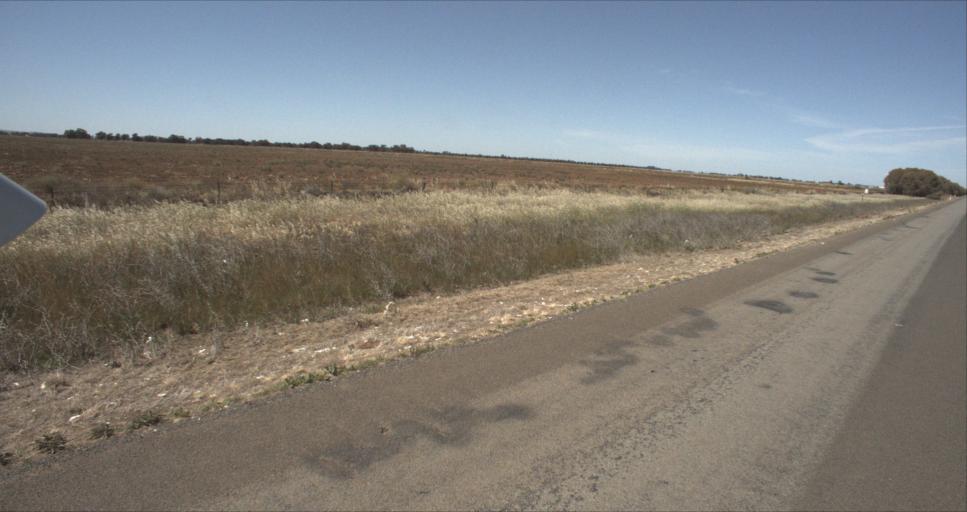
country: AU
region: New South Wales
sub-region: Leeton
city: Leeton
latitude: -34.4795
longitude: 146.2908
